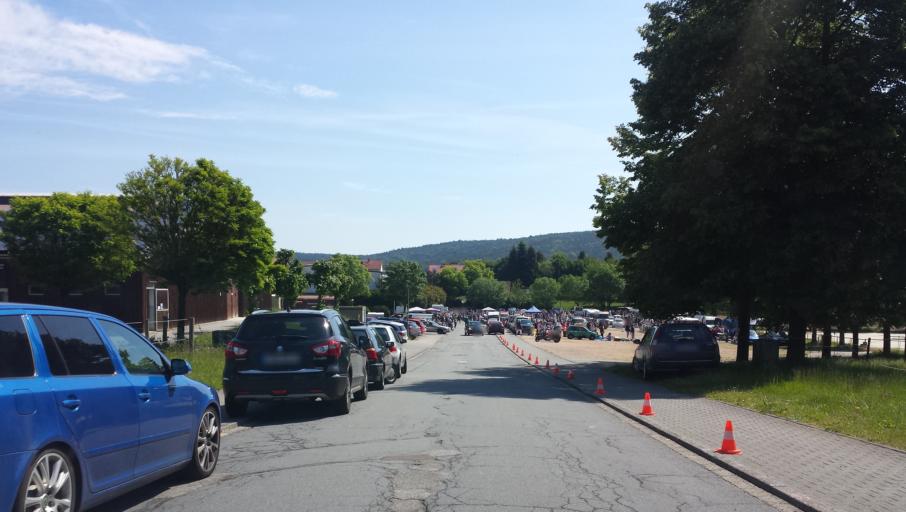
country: DE
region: Hesse
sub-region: Regierungsbezirk Darmstadt
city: Beerfelden
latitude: 49.5636
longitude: 8.9719
